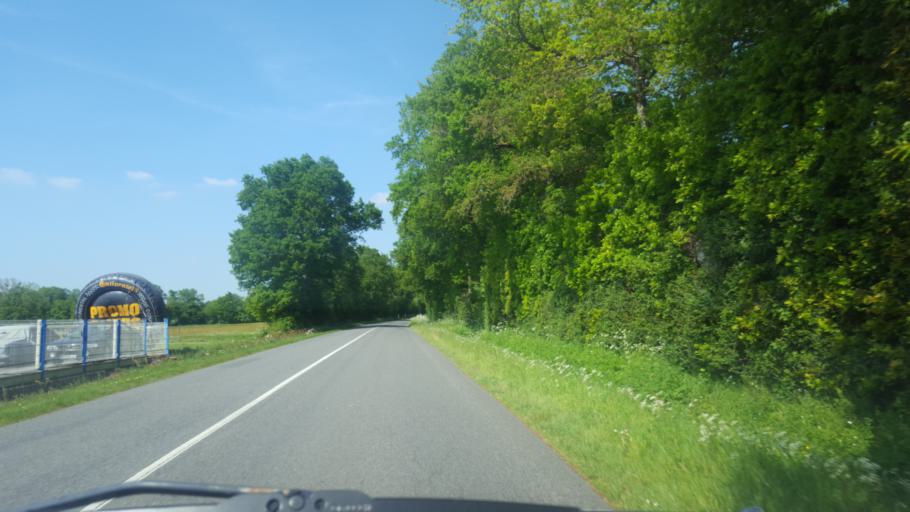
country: FR
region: Pays de la Loire
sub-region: Departement de la Loire-Atlantique
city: La Limouziniere
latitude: 46.9729
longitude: -1.5724
